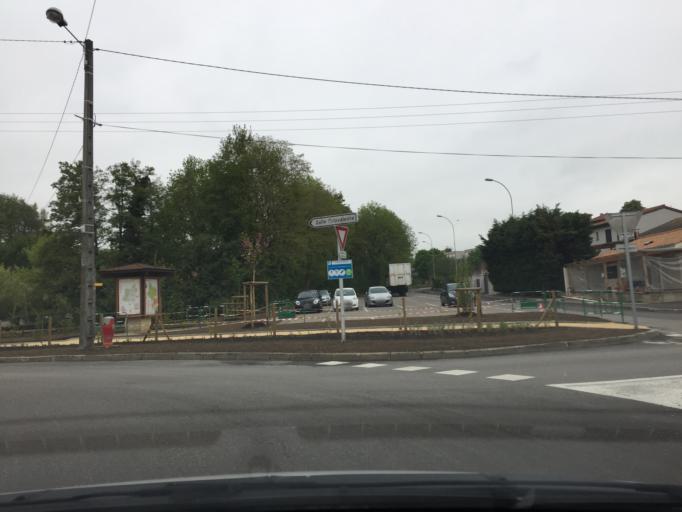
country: FR
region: Rhone-Alpes
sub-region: Departement du Rhone
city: Mornant
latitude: 45.6160
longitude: 4.6707
